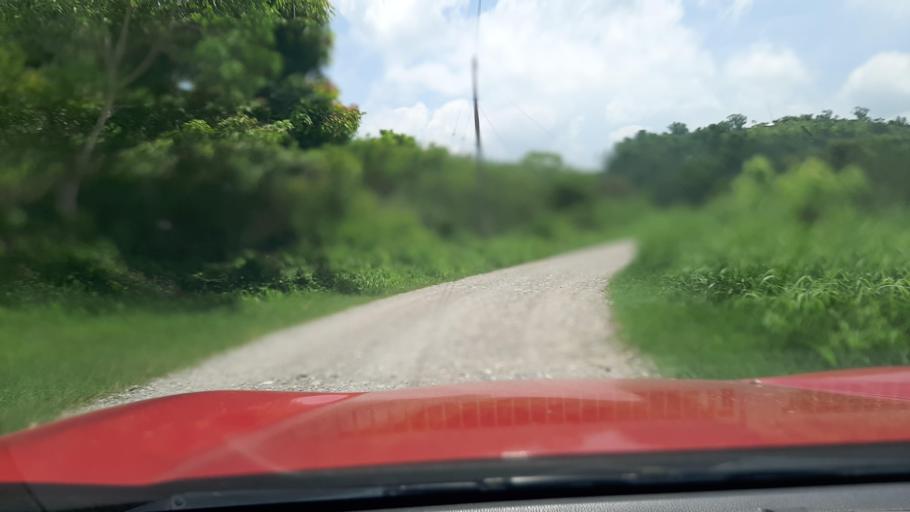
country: MX
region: Veracruz
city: Papantla de Olarte
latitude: 20.4253
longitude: -97.2646
